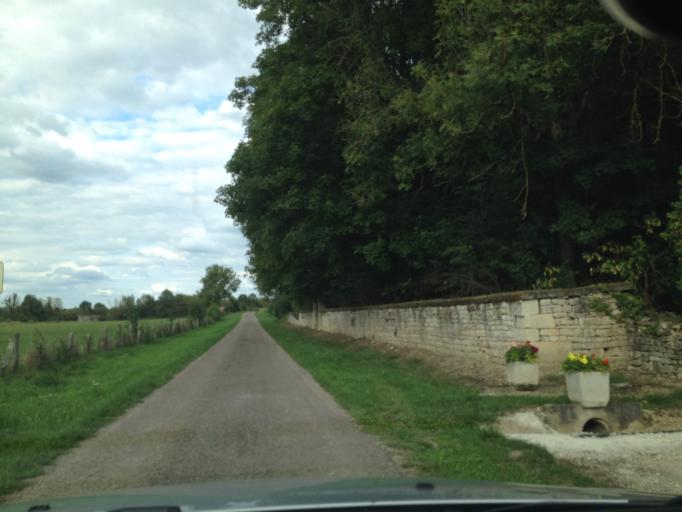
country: FR
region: Franche-Comte
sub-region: Departement de la Haute-Saone
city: Jussey
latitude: 47.8926
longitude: 5.9831
